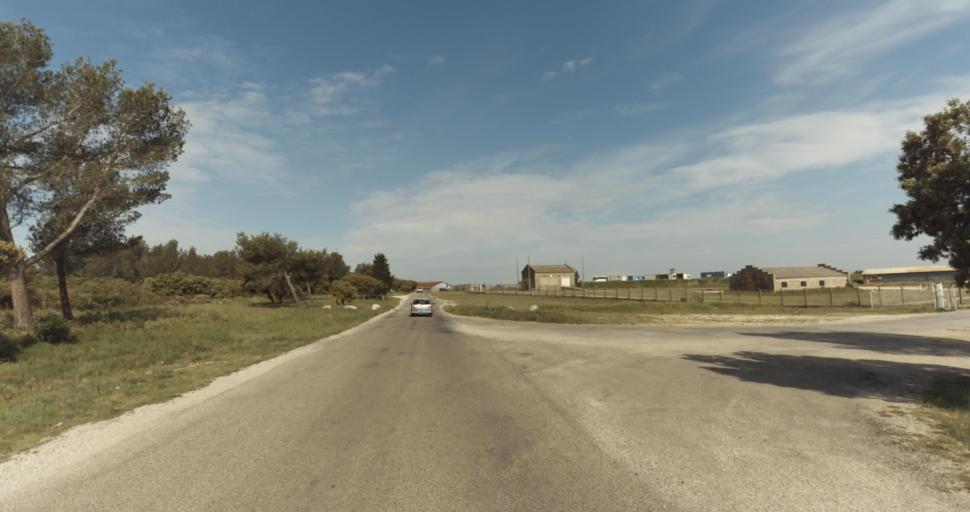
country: FR
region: Languedoc-Roussillon
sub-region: Departement du Gard
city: Poulx
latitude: 43.8826
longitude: 4.3854
